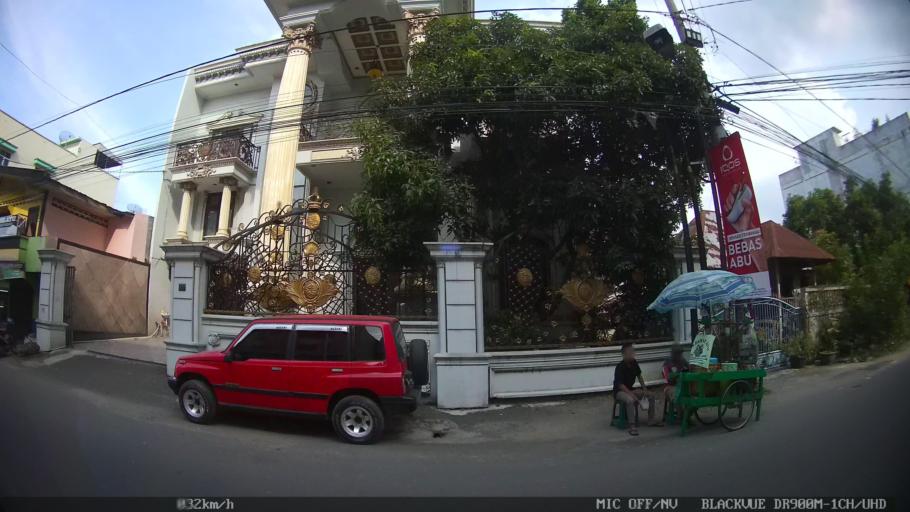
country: ID
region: North Sumatra
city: Binjai
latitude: 3.6022
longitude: 98.4864
